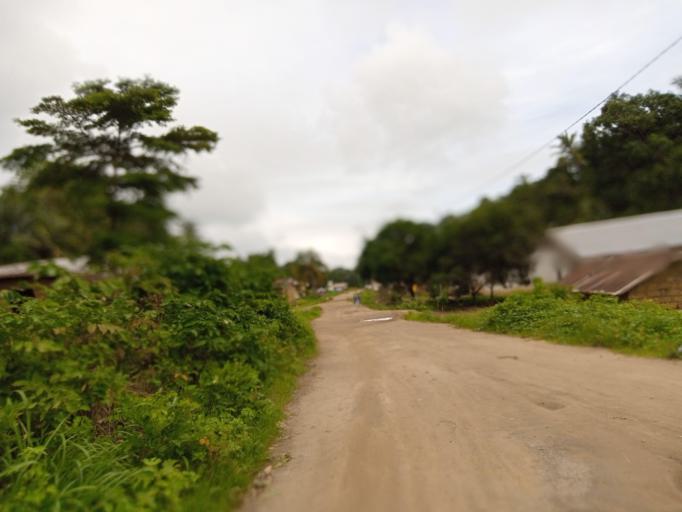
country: SL
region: Northern Province
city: Masoyila
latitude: 8.5959
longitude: -13.1982
